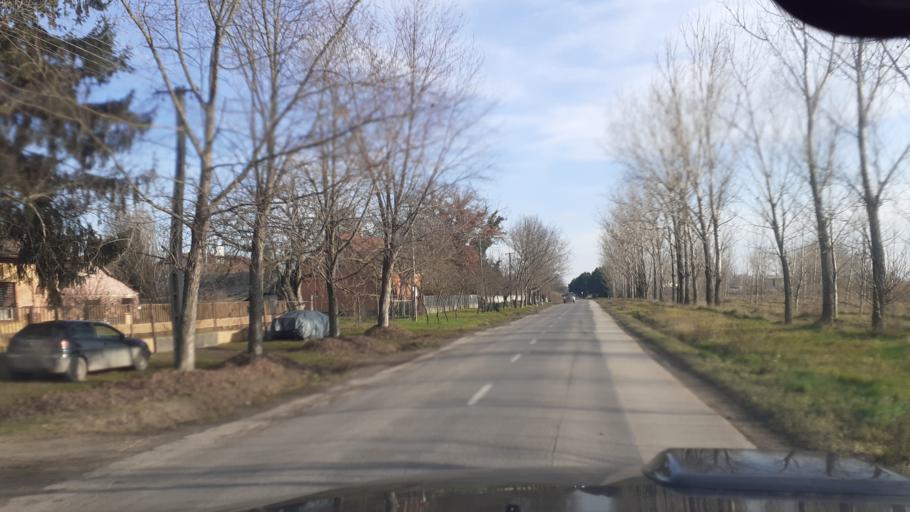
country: HU
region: Pest
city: Domsod
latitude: 47.0901
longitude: 19.0287
